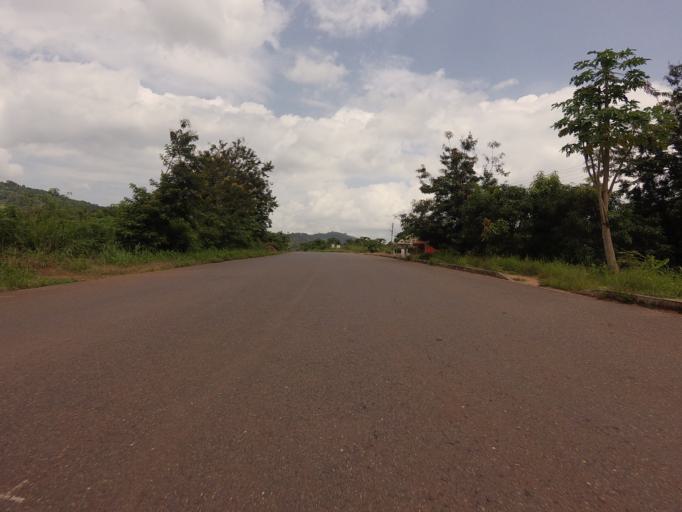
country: GH
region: Volta
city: Ho
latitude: 6.5203
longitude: 0.2198
